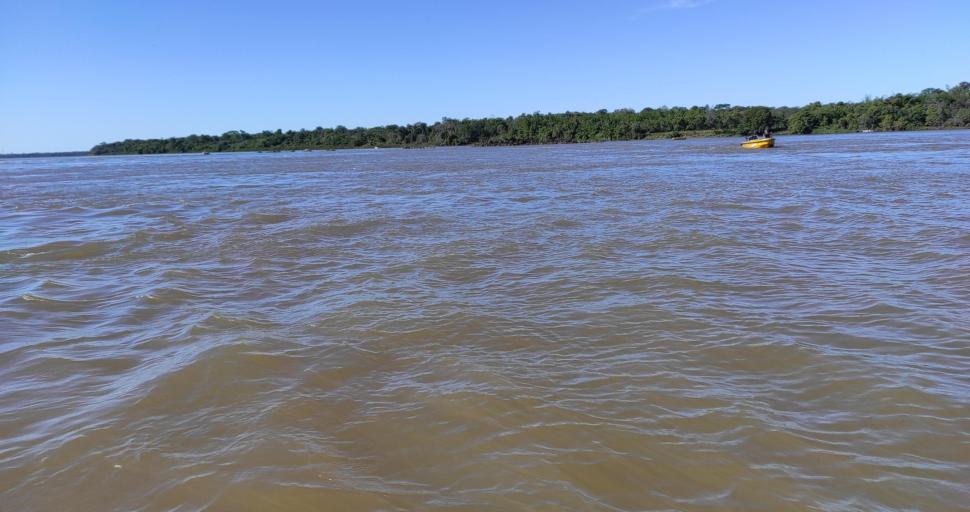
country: AR
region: Corrientes
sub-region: Departamento de Itati
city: Itati
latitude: -27.2772
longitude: -58.3240
